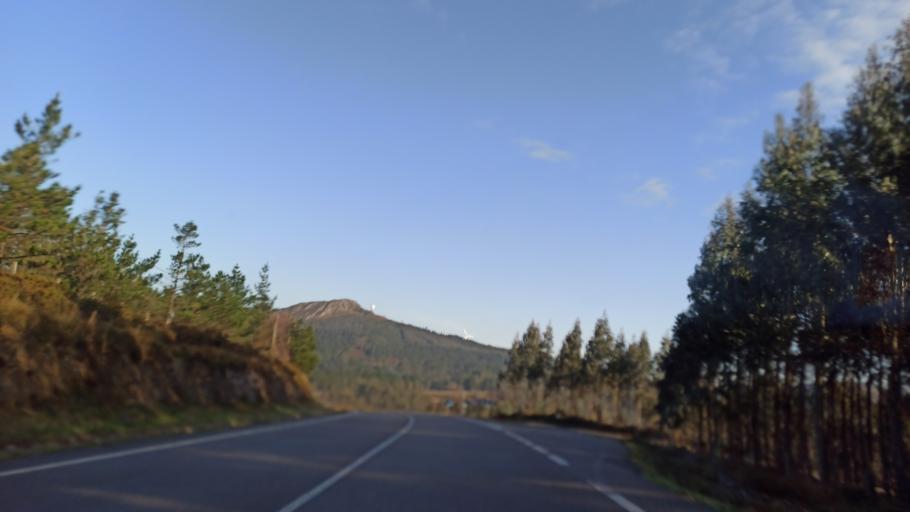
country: ES
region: Galicia
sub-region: Provincia da Coruna
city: As Pontes de Garcia Rodriguez
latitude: 43.4956
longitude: -7.8309
